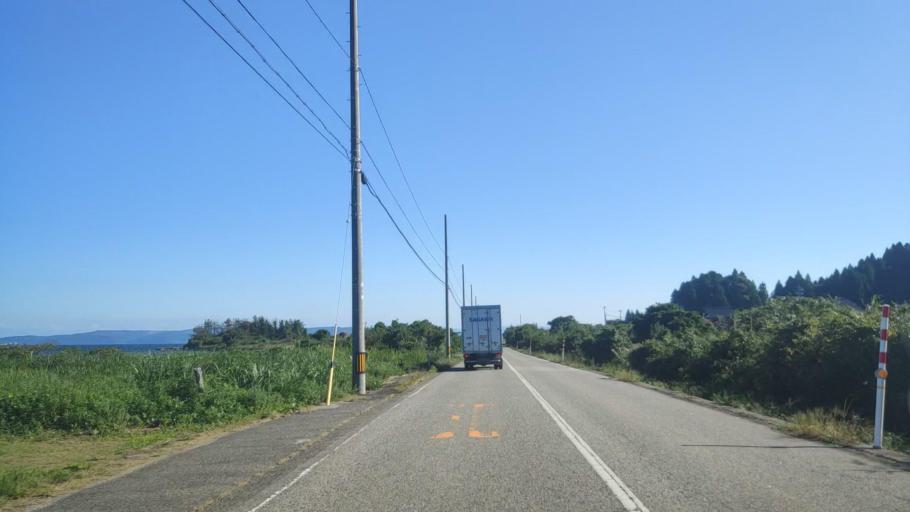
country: JP
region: Ishikawa
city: Nanao
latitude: 37.1974
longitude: 136.9101
